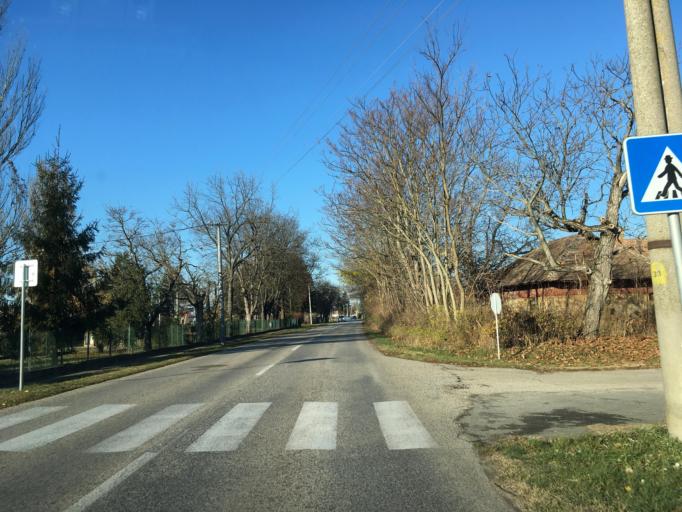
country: SK
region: Nitriansky
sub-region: Okres Komarno
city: Hurbanovo
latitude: 47.9045
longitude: 18.1362
